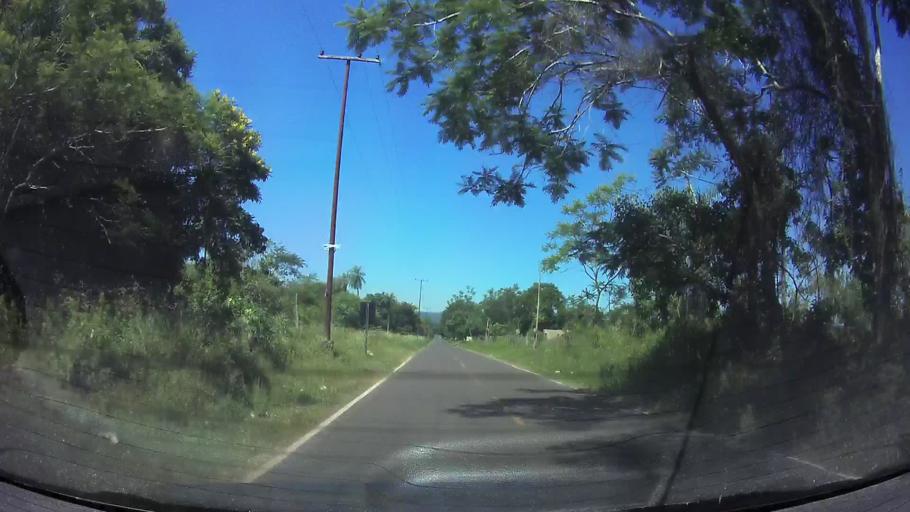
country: PY
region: Central
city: Aregua
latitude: -25.2876
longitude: -57.4047
